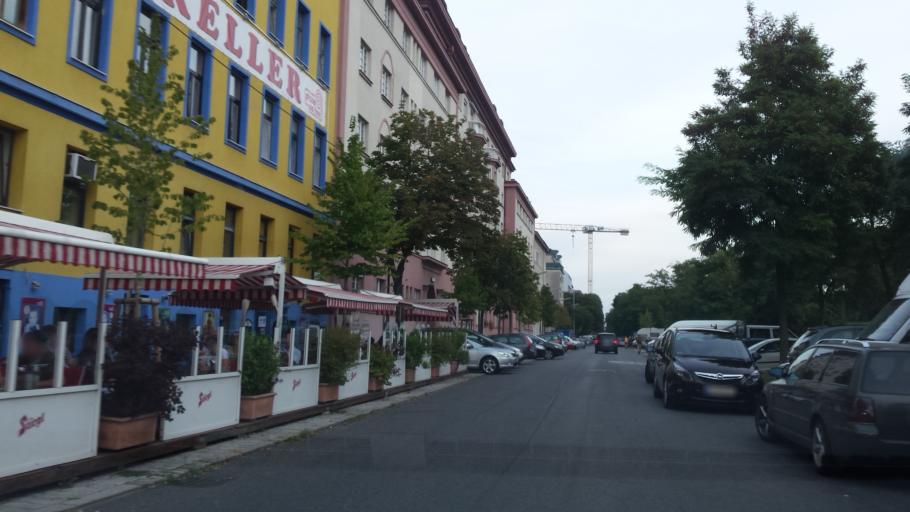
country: AT
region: Vienna
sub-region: Wien Stadt
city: Vienna
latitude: 48.2261
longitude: 16.4199
